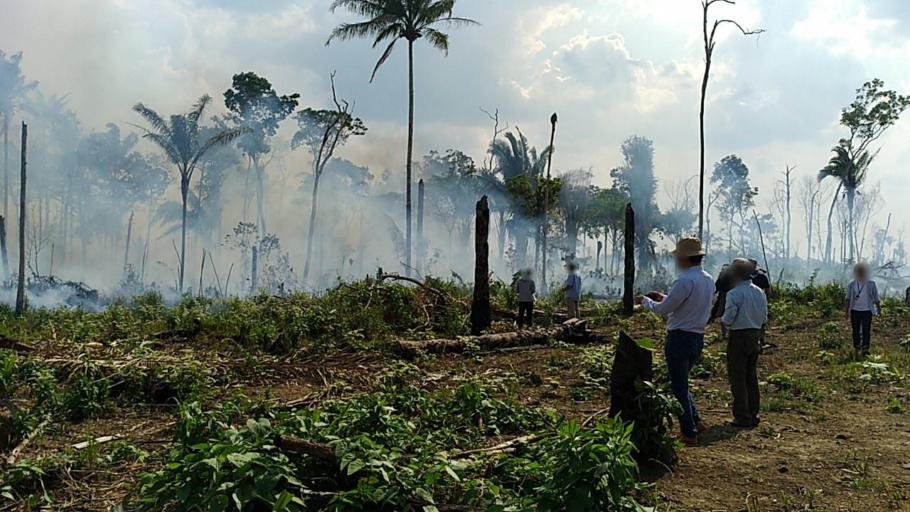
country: BR
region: Rondonia
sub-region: Porto Velho
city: Porto Velho
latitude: -8.6639
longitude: -64.0237
